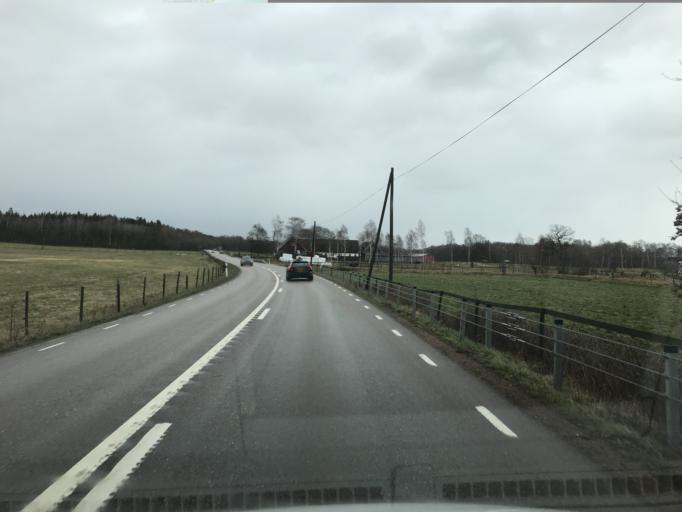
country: SE
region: Skane
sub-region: Klippans Kommun
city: Ljungbyhed
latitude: 56.0960
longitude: 13.1875
